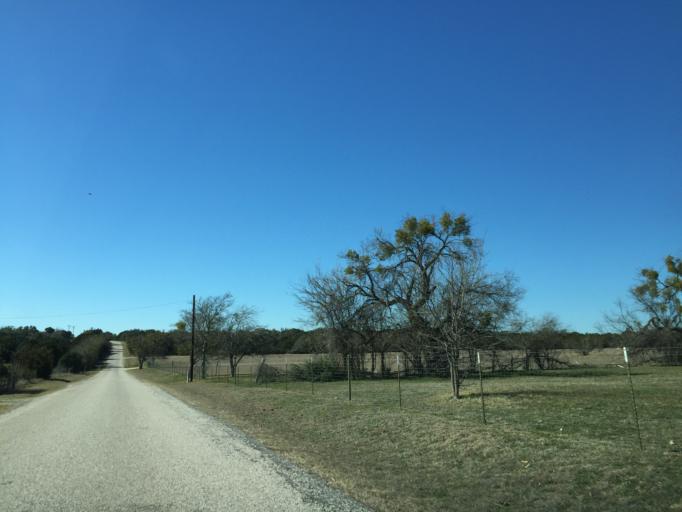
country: US
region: Texas
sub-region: Lampasas County
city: Kempner
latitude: 30.9341
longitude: -98.0315
